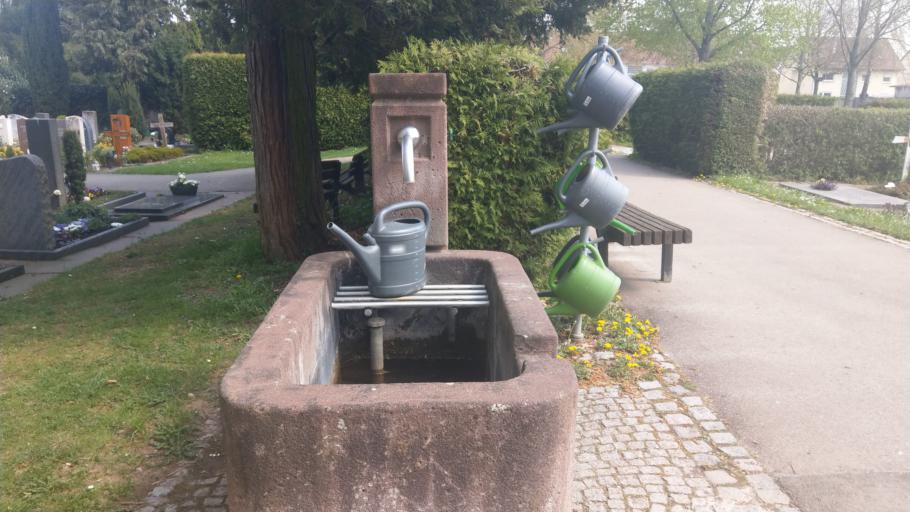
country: DE
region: Baden-Wuerttemberg
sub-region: Regierungsbezirk Stuttgart
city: Filderstadt
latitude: 48.6778
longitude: 9.2199
